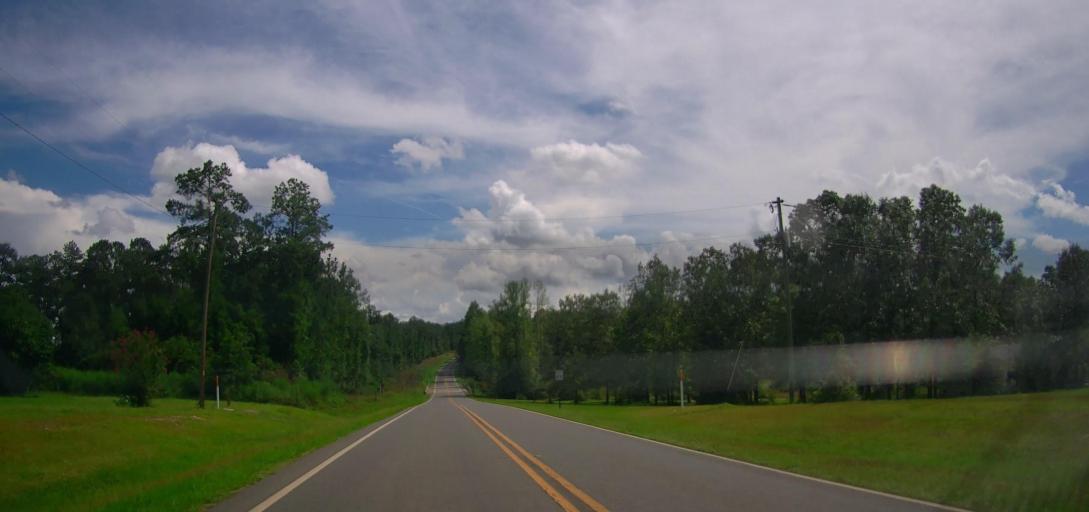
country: US
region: Georgia
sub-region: Taylor County
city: Butler
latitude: 32.5316
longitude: -84.2104
